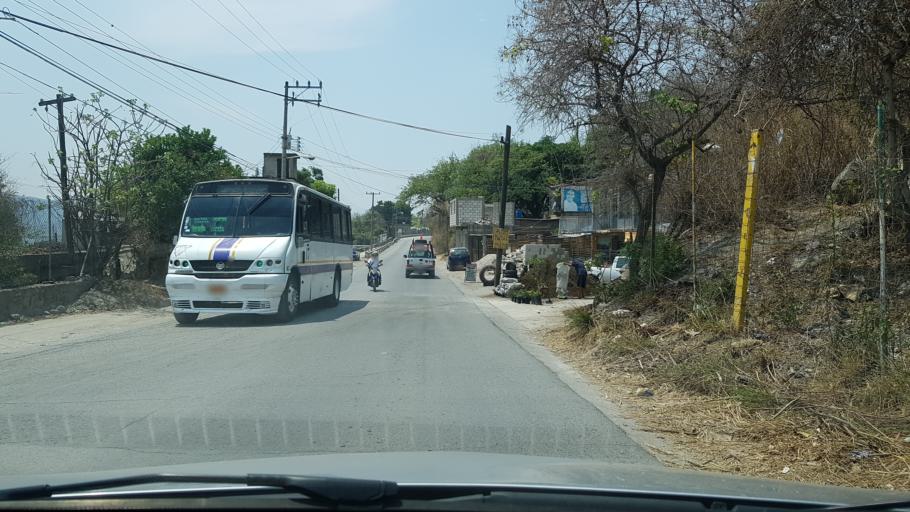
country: MX
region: Morelos
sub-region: Jiutepec
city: Calera Chica
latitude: 18.8661
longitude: -99.1743
